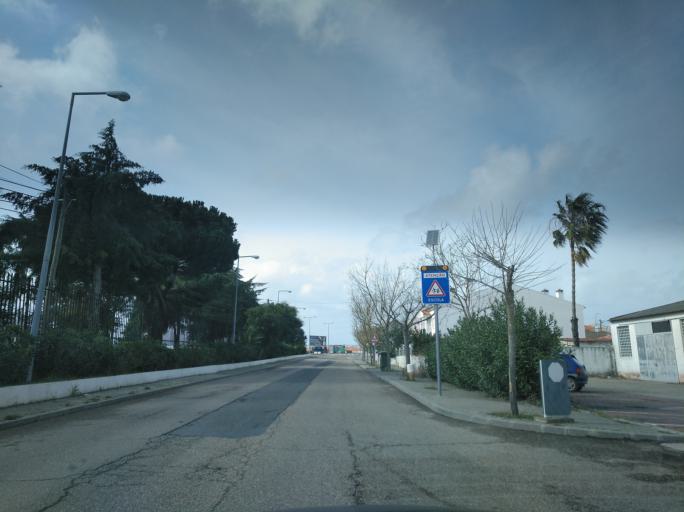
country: PT
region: Setubal
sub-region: Grandola
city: Grandola
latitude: 38.1709
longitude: -8.5572
